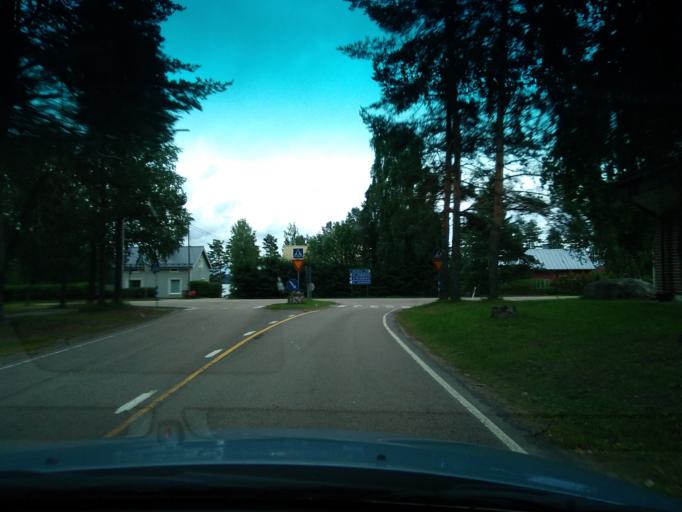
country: FI
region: Central Finland
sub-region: Keuruu
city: Multia
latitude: 62.4097
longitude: 24.7995
